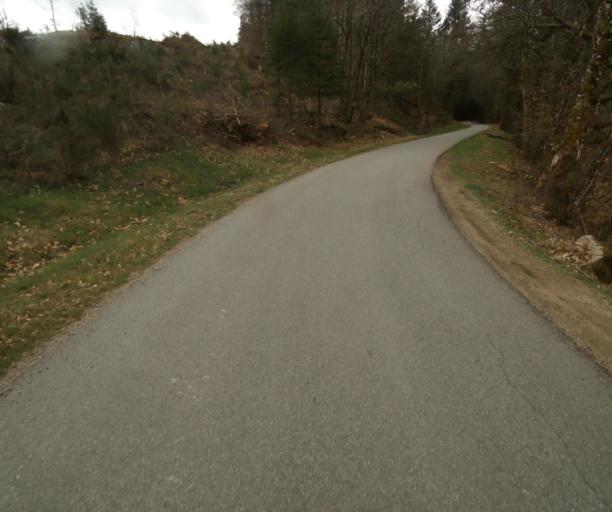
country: FR
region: Limousin
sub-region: Departement de la Correze
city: Correze
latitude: 45.3233
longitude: 1.9434
